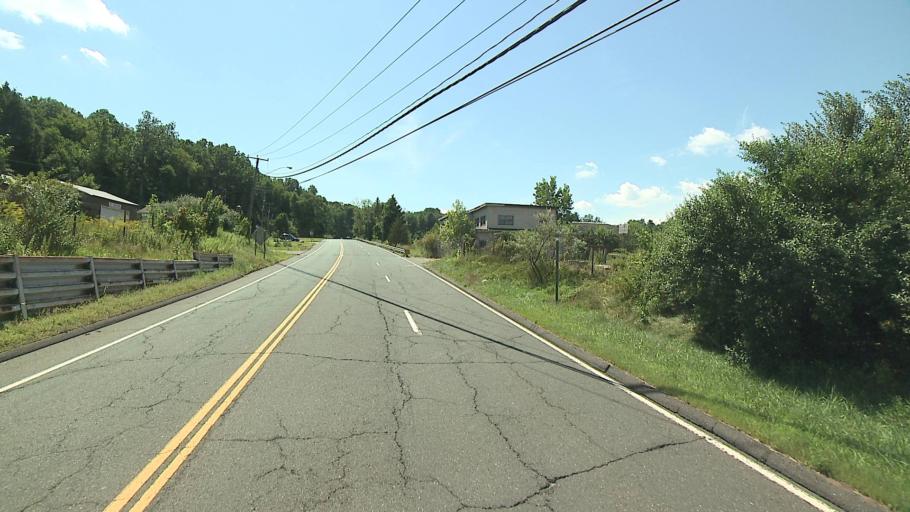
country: US
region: Connecticut
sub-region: New Haven County
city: Oxford
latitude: 41.3865
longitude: -73.1890
